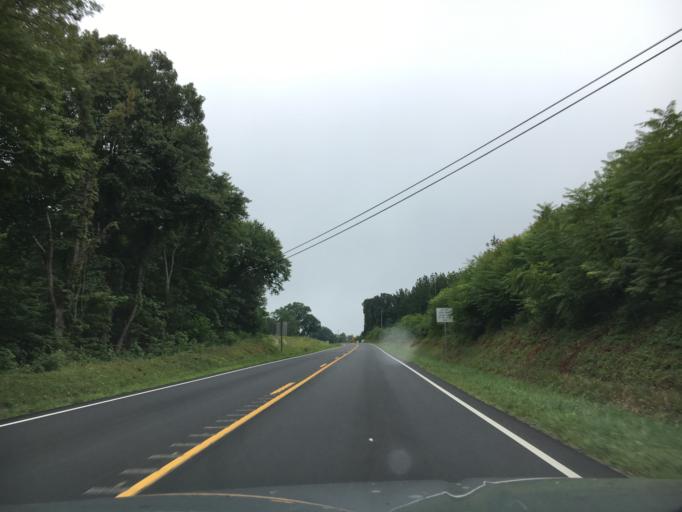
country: US
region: Virginia
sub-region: Campbell County
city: Brookneal
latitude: 37.0307
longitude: -78.9521
